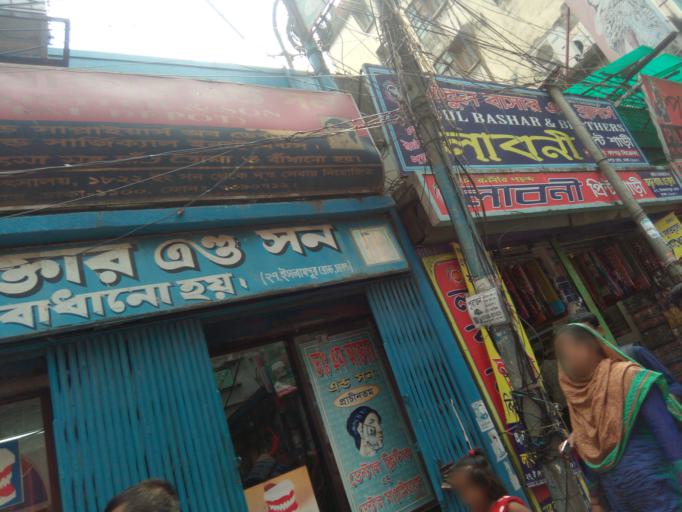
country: BD
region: Dhaka
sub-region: Dhaka
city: Dhaka
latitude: 23.7112
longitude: 90.4049
